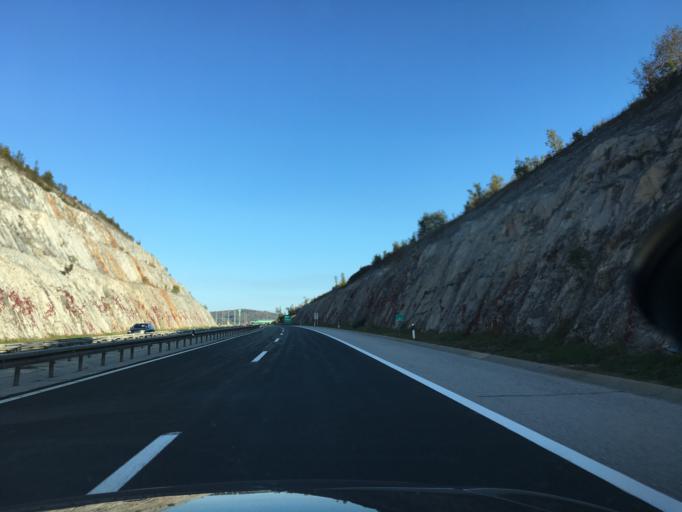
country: HR
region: Licko-Senjska
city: Otocac
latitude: 44.7450
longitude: 15.3778
